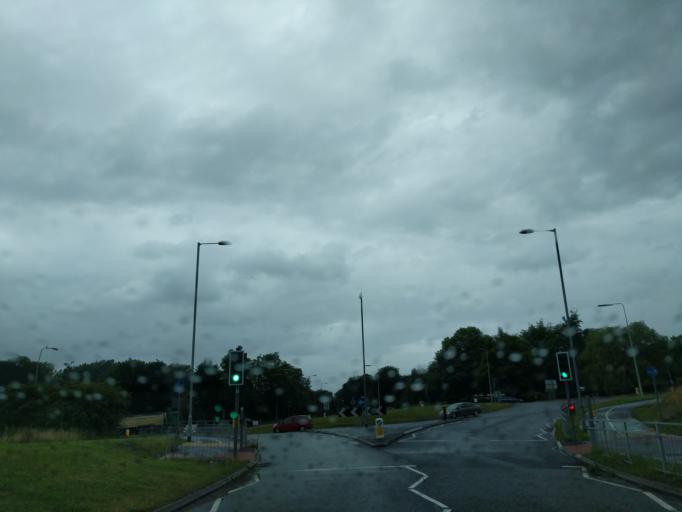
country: GB
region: England
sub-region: Staffordshire
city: Stafford
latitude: 52.8107
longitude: -2.0838
